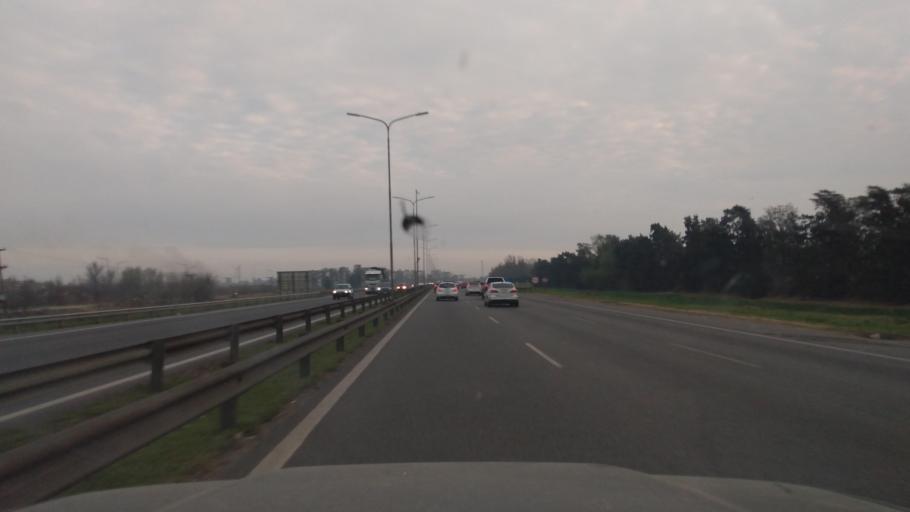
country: AR
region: Buenos Aires
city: Hurlingham
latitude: -34.5417
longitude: -58.6012
